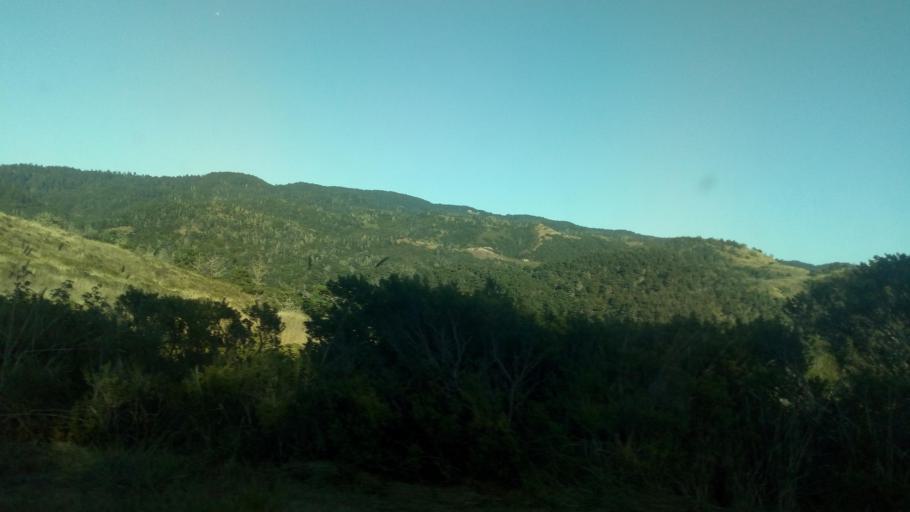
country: US
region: California
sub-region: Marin County
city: Inverness
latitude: 38.0387
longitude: -122.8725
